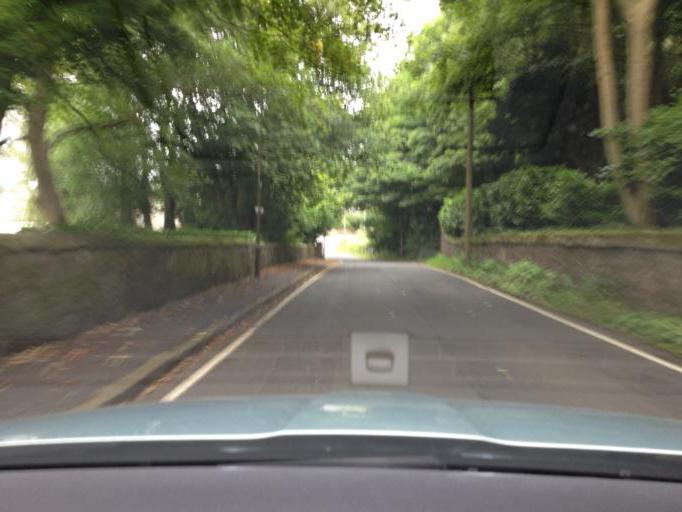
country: GB
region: Scotland
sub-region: West Lothian
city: Bathgate
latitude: 55.9317
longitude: -3.6572
